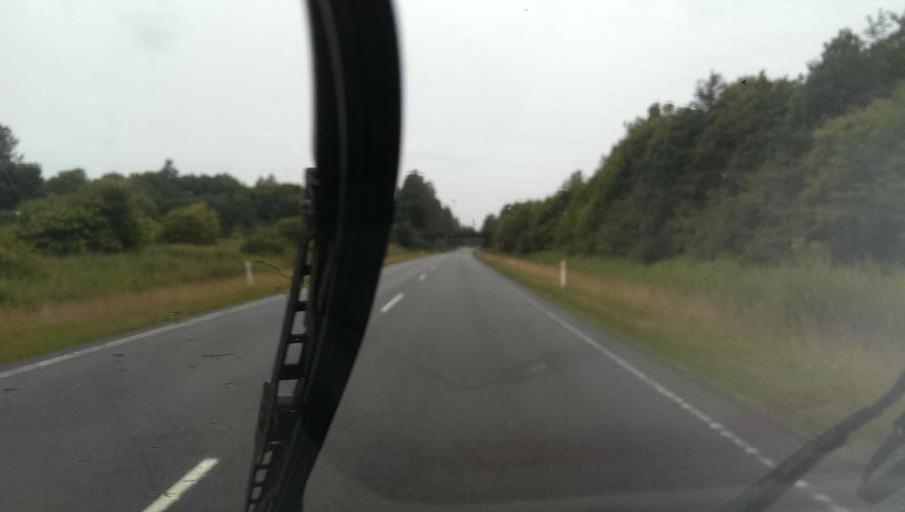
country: DK
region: South Denmark
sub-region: Esbjerg Kommune
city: Esbjerg
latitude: 55.5224
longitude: 8.4523
